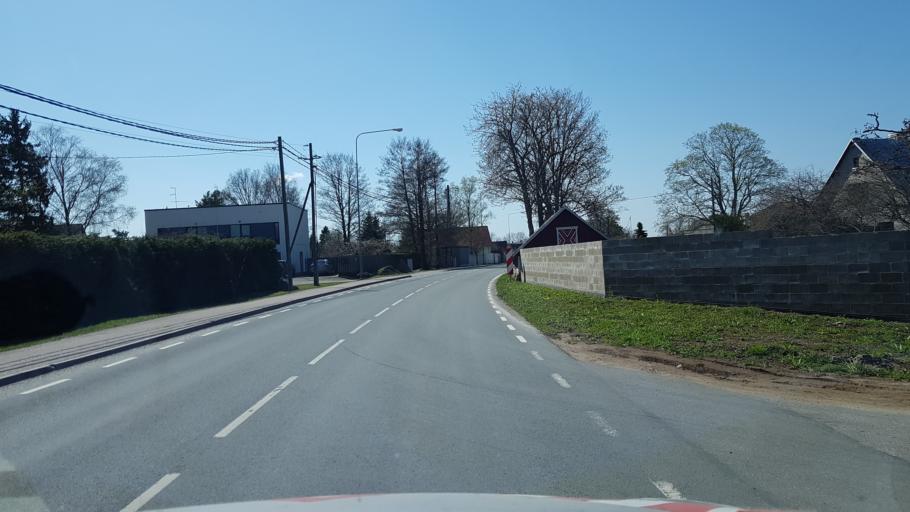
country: EE
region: Harju
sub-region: Viimsi vald
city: Rummu
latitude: 59.5583
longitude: 24.7975
